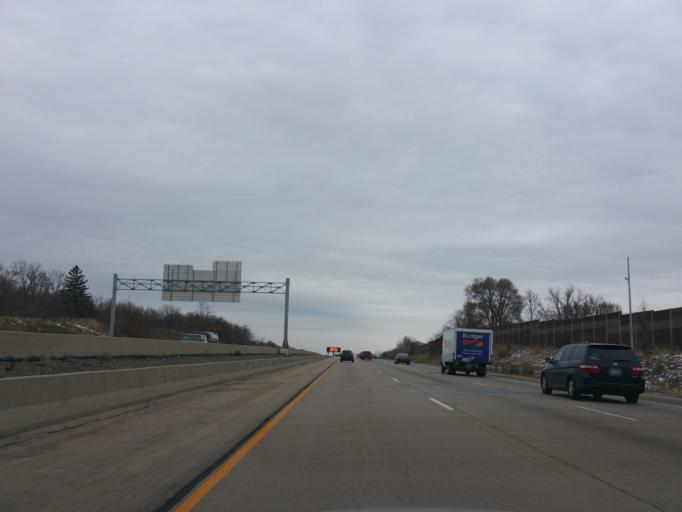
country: US
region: Wisconsin
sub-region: Dane County
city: Monona
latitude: 43.0842
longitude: -89.2836
